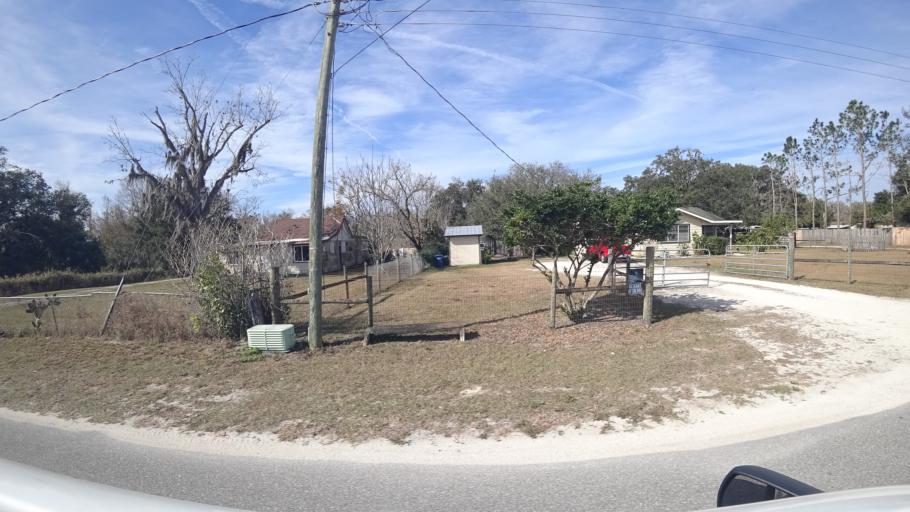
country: US
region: Florida
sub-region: Manatee County
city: Ellenton
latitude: 27.5722
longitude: -82.4277
